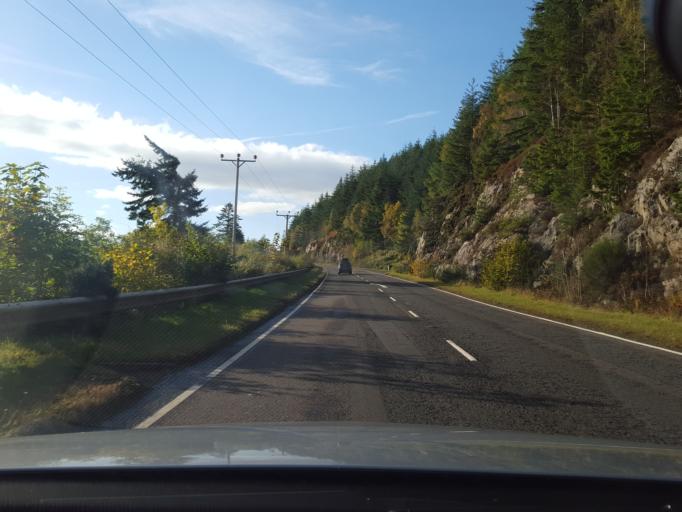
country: GB
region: Scotland
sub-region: Highland
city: Beauly
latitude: 57.2269
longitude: -4.5711
